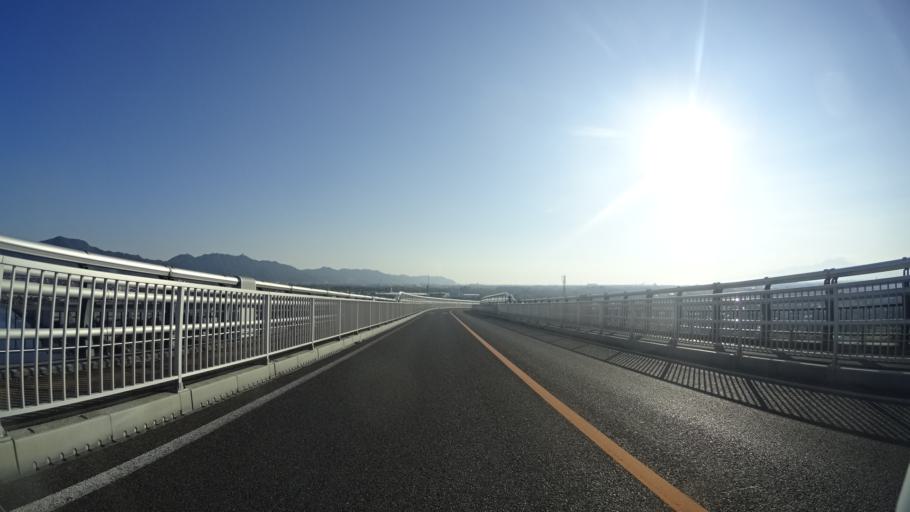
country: JP
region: Shimane
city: Sakaiminato
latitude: 35.5196
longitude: 133.2012
